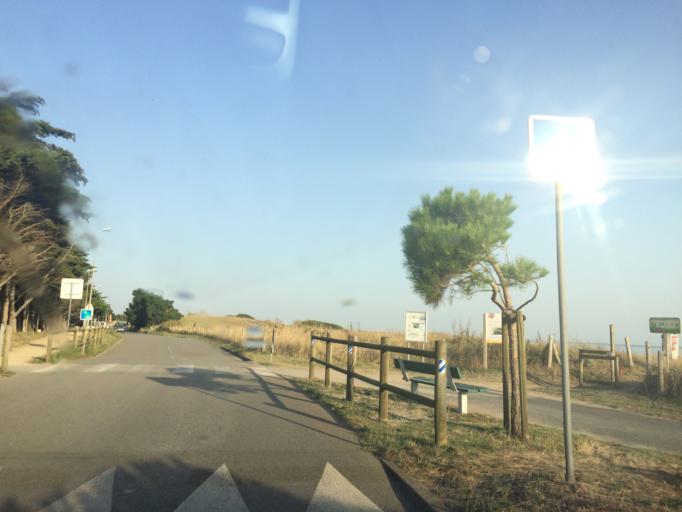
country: FR
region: Brittany
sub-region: Departement du Morbihan
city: Damgan
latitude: 47.5164
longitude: -2.5677
